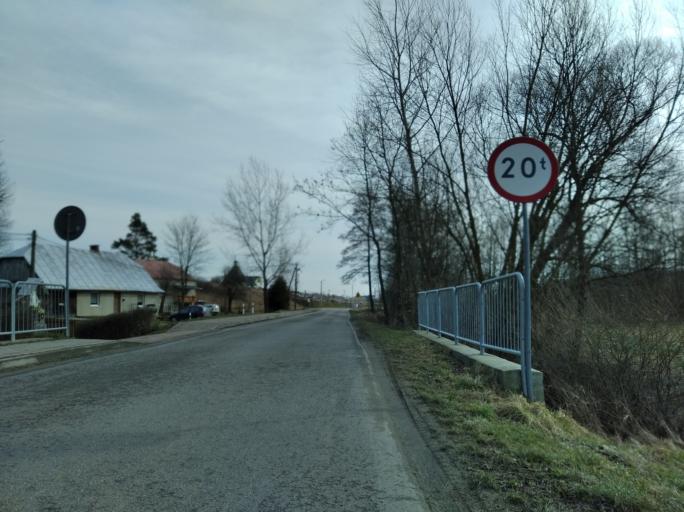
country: PL
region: Subcarpathian Voivodeship
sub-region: Powiat brzozowski
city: Orzechowka
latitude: 49.7266
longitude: 21.9493
